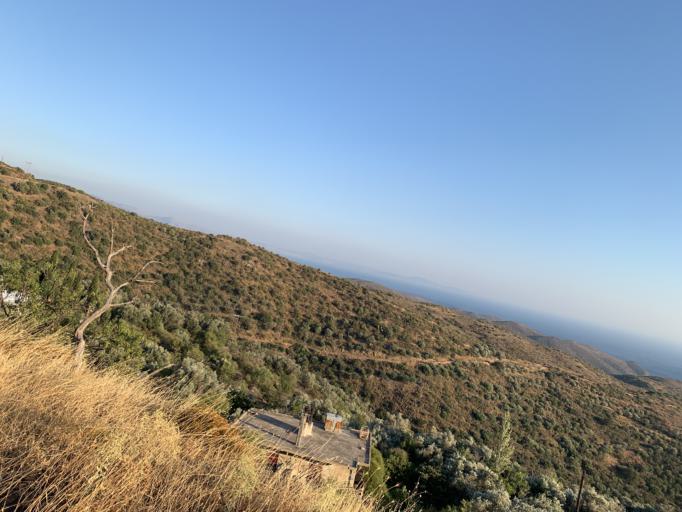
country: GR
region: North Aegean
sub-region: Chios
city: Vrontados
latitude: 38.5274
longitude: 25.8665
